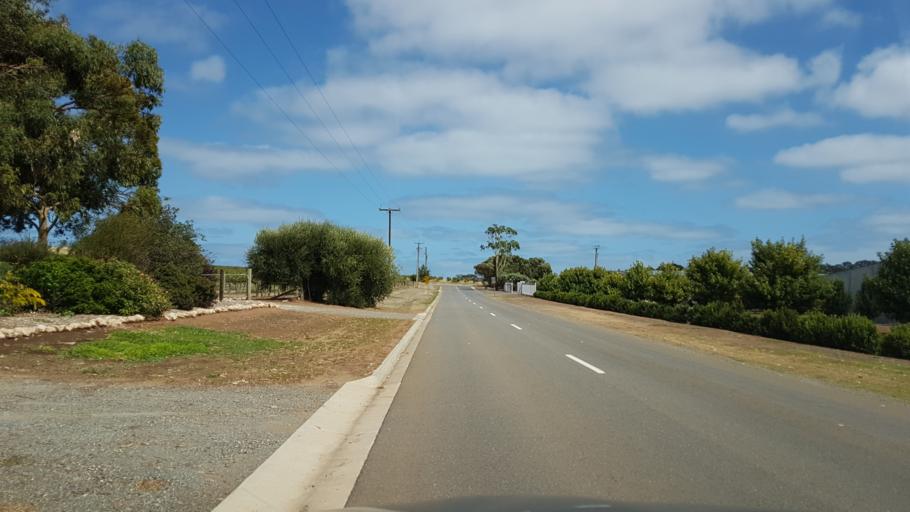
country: AU
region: South Australia
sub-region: Onkaparinga
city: McLaren Vale
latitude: -35.2104
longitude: 138.5196
